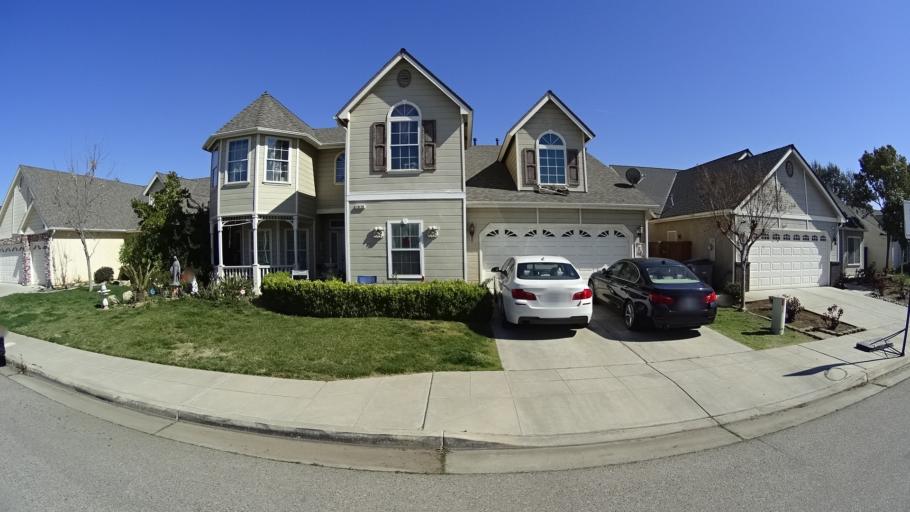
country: US
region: California
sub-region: Fresno County
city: Clovis
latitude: 36.8507
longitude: -119.7442
